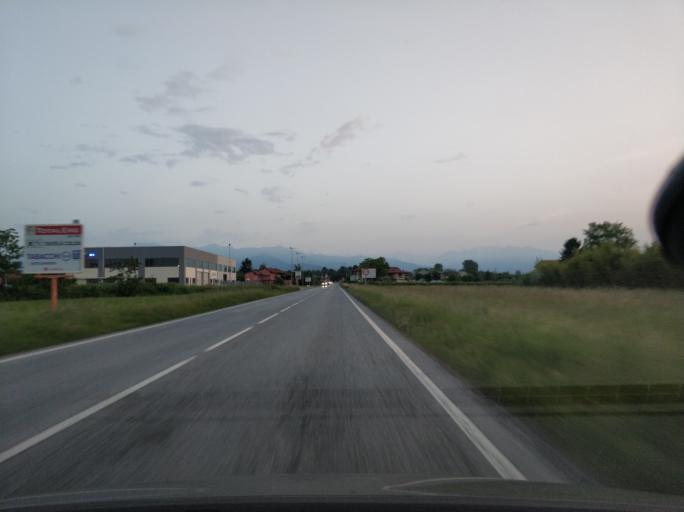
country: IT
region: Piedmont
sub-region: Provincia di Torino
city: San Maurizio
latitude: 45.2002
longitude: 7.6386
